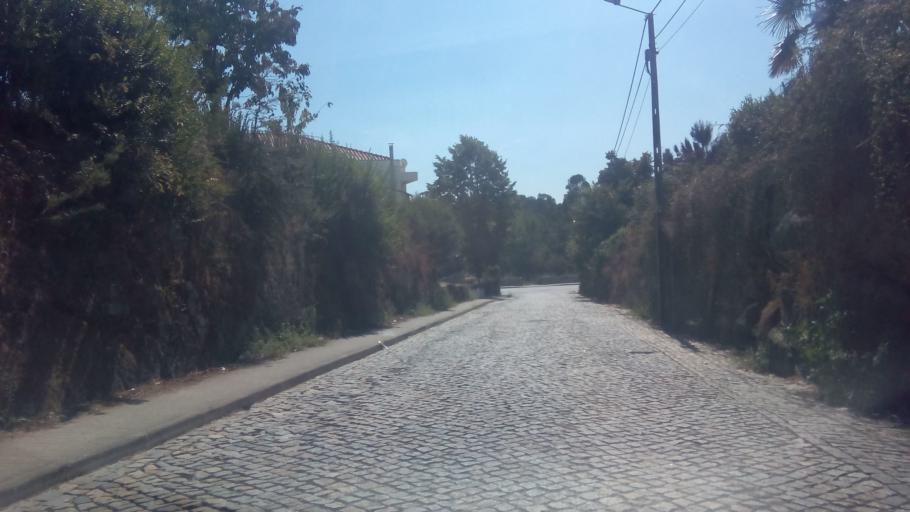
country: PT
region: Porto
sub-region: Paredes
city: Paredes
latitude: 41.2036
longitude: -8.3193
